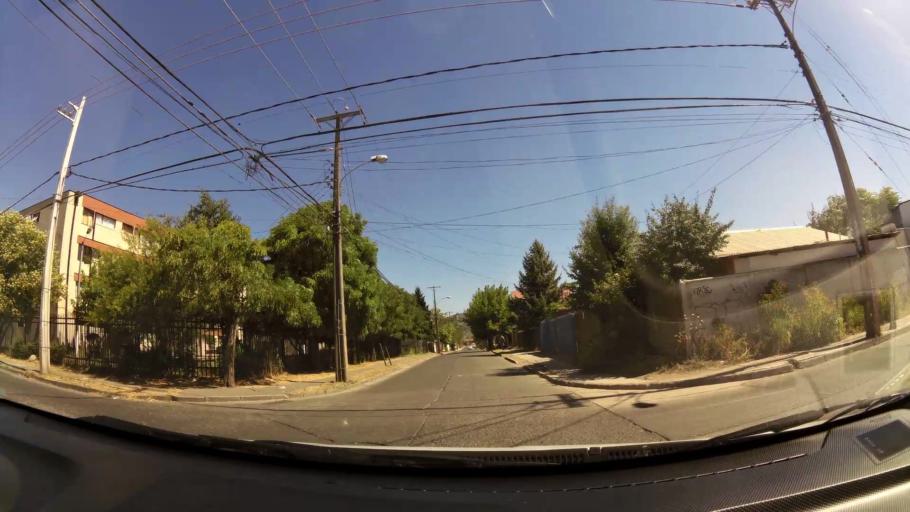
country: CL
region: O'Higgins
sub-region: Provincia de Colchagua
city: Chimbarongo
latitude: -34.5908
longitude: -70.9956
